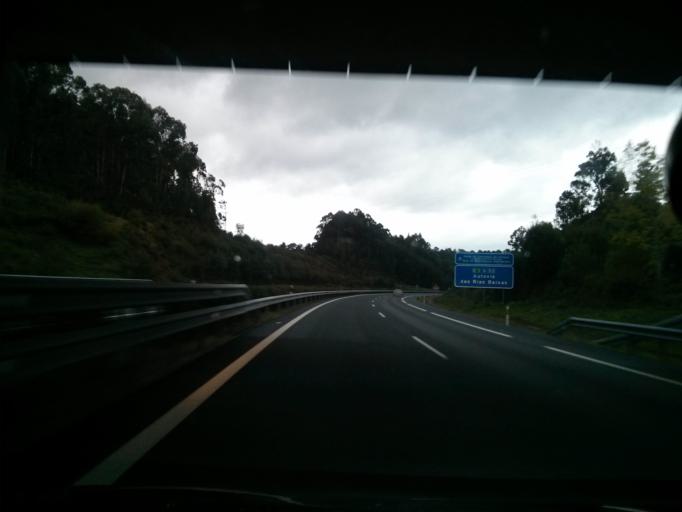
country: ES
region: Galicia
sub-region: Provincia de Pontevedra
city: Ponteareas
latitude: 42.1496
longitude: -8.4284
